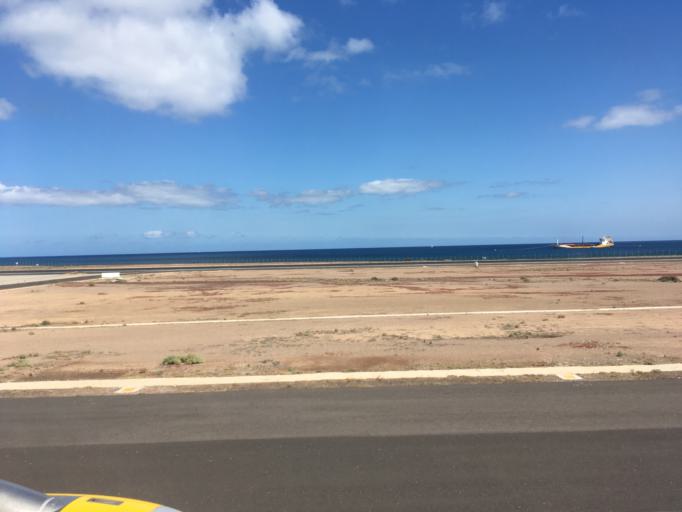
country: ES
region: Canary Islands
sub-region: Provincia de Las Palmas
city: Tias
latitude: 28.9436
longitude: -13.6083
